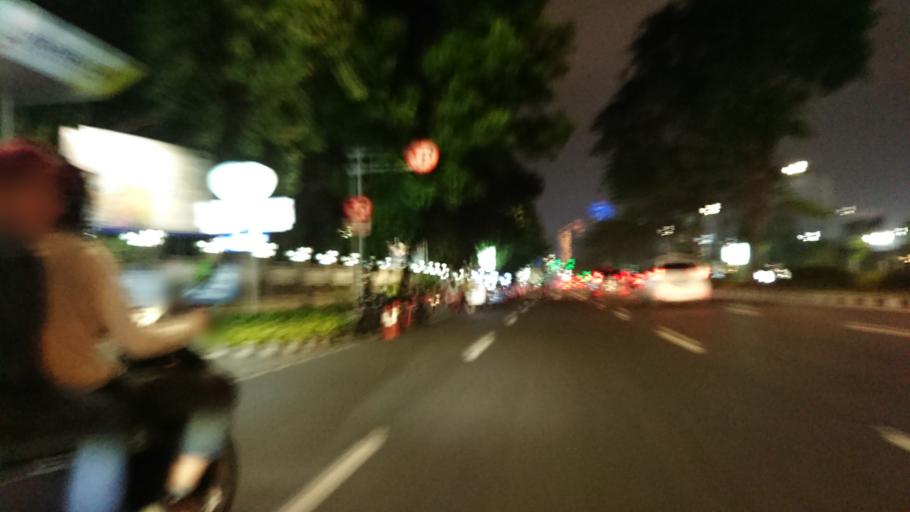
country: ID
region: Jakarta Raya
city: Jakarta
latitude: -6.2137
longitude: 106.8010
